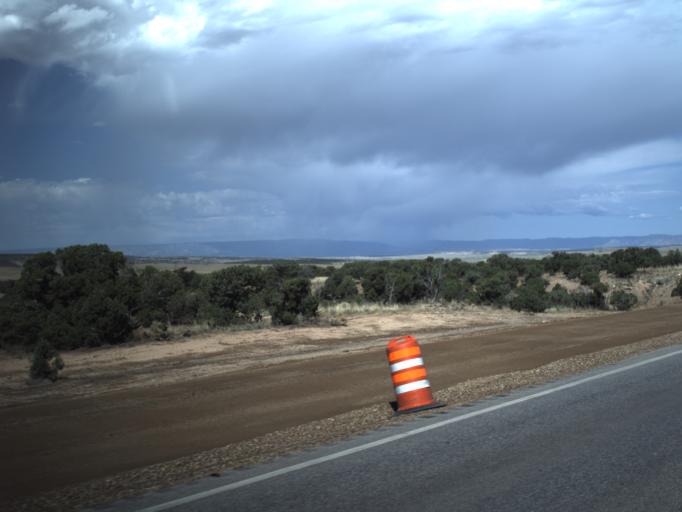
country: US
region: Utah
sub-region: Carbon County
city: East Carbon City
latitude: 39.4211
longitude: -110.4417
